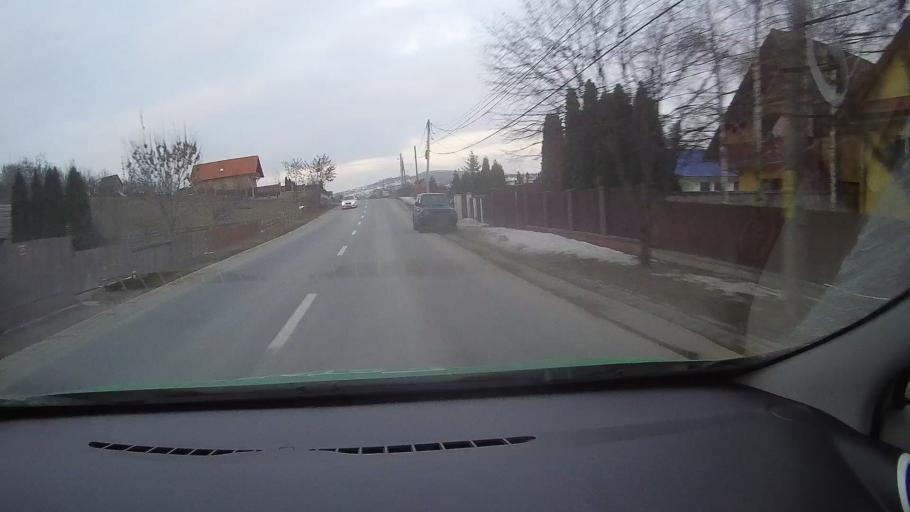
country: RO
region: Harghita
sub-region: Comuna Lupeni
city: Lupeni
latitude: 46.3580
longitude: 25.2296
